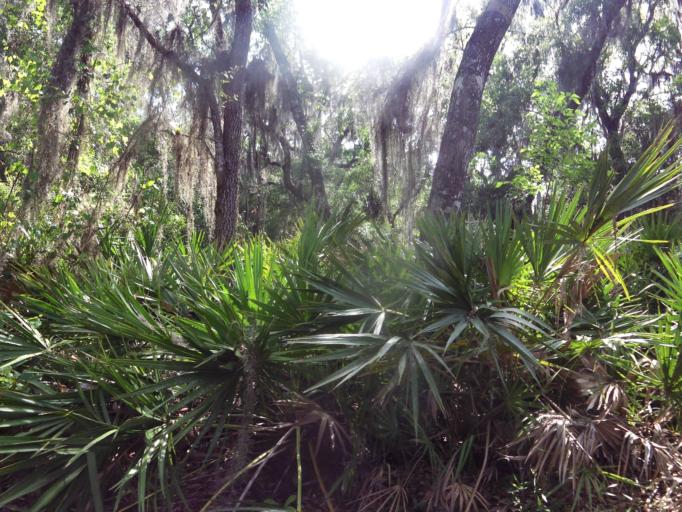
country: US
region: Florida
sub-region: Duval County
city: Atlantic Beach
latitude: 30.4900
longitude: -81.4898
